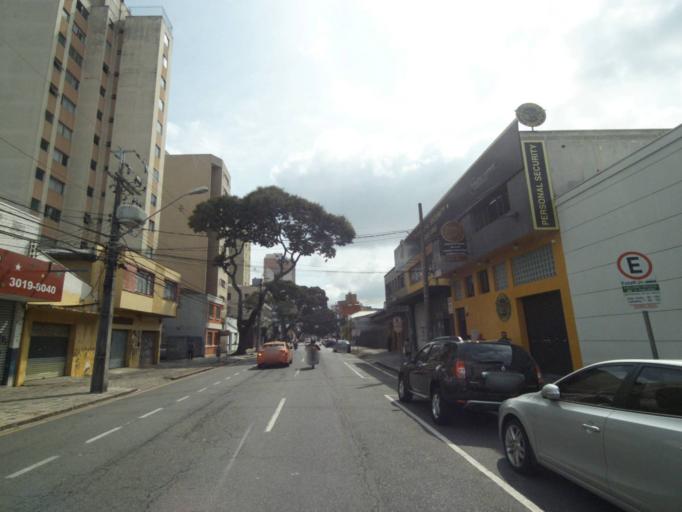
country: BR
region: Parana
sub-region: Curitiba
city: Curitiba
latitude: -25.4342
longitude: -49.2586
